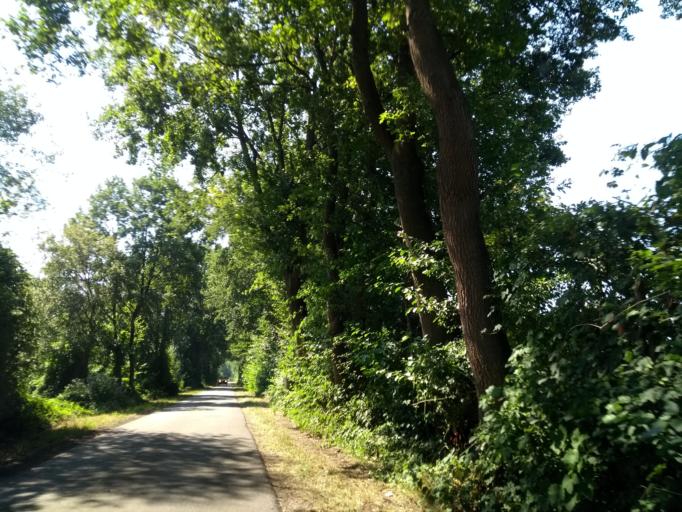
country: DE
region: North Rhine-Westphalia
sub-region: Regierungsbezirk Arnsberg
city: Lippstadt
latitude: 51.7243
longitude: 8.4112
